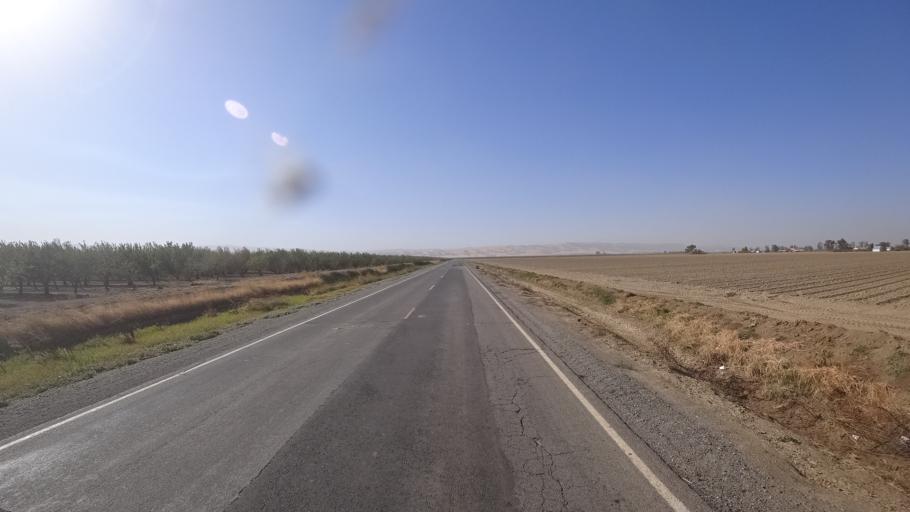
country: US
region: California
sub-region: Yolo County
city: Esparto
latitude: 38.7315
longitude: -121.9933
